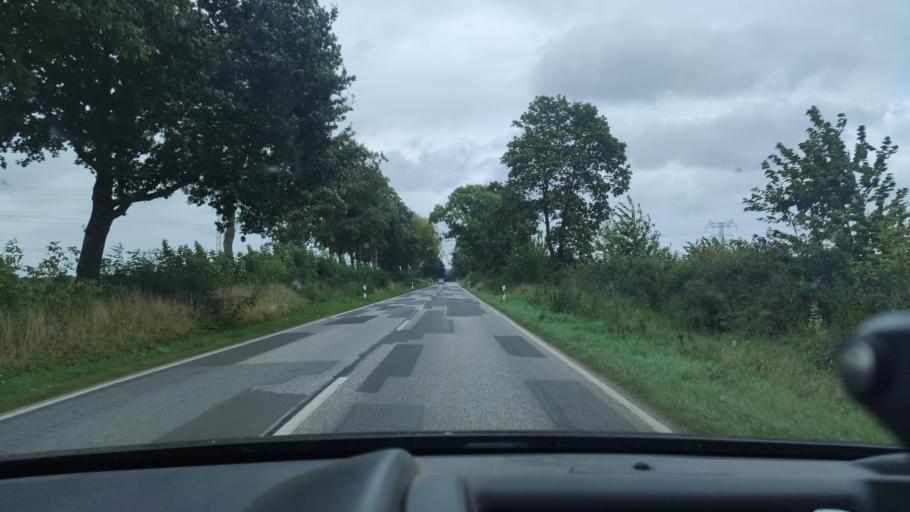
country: DE
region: Mecklenburg-Vorpommern
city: Guestrow
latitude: 53.8390
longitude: 12.1264
